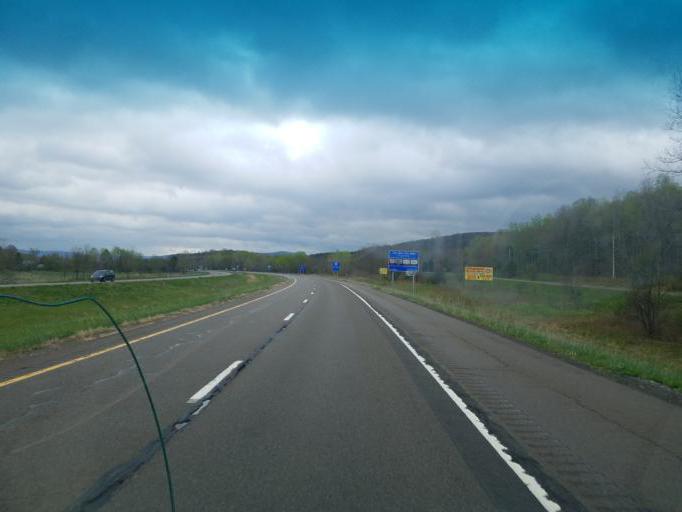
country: US
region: New York
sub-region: Cattaraugus County
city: Randolph
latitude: 42.1047
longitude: -78.9127
